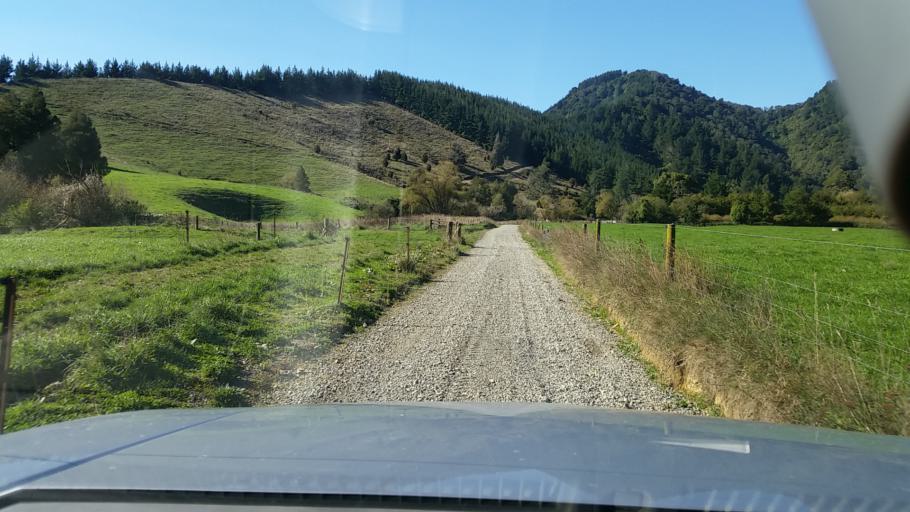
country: NZ
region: Nelson
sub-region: Nelson City
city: Nelson
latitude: -41.2217
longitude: 173.6089
